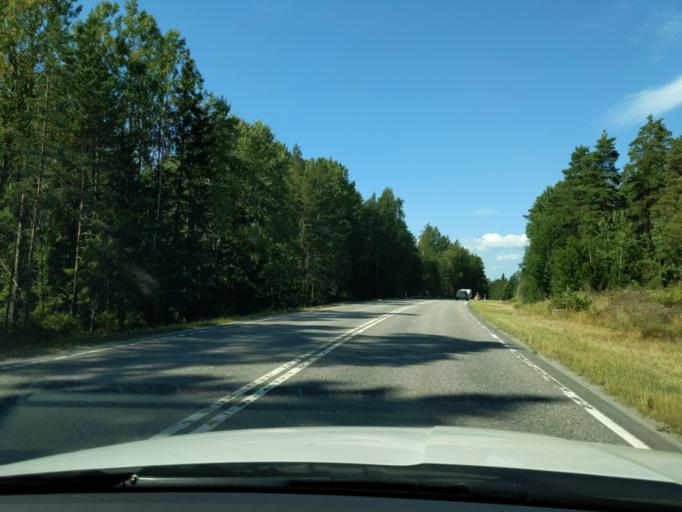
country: FI
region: Uusimaa
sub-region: Raaseporin
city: Ekenaes
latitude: 60.0197
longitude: 23.3782
